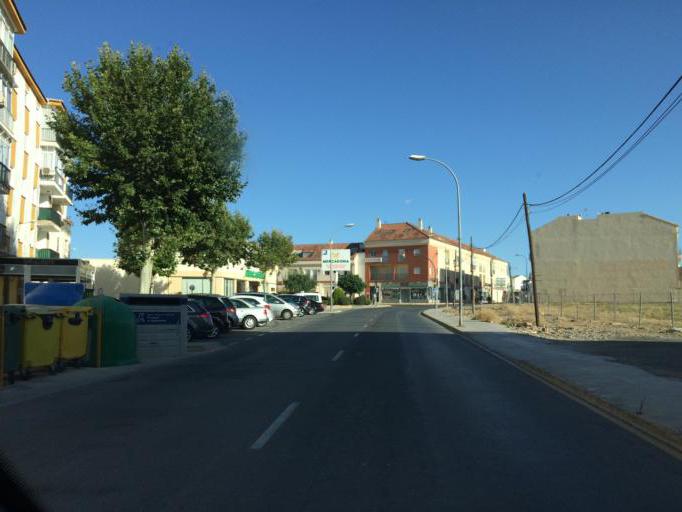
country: ES
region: Andalusia
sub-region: Provincia de Malaga
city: Campillos
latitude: 37.0458
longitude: -4.8650
